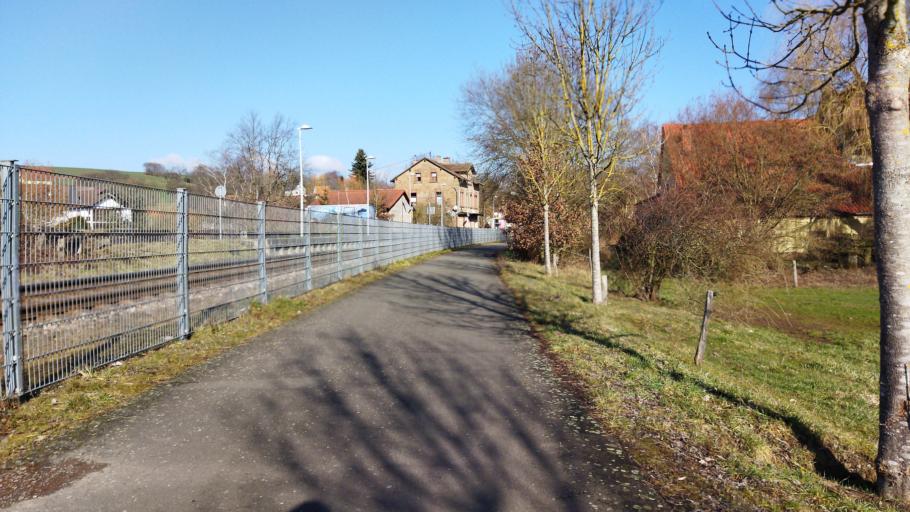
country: DE
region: Rheinland-Pfalz
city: Rehweiler
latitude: 49.4842
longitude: 7.4407
